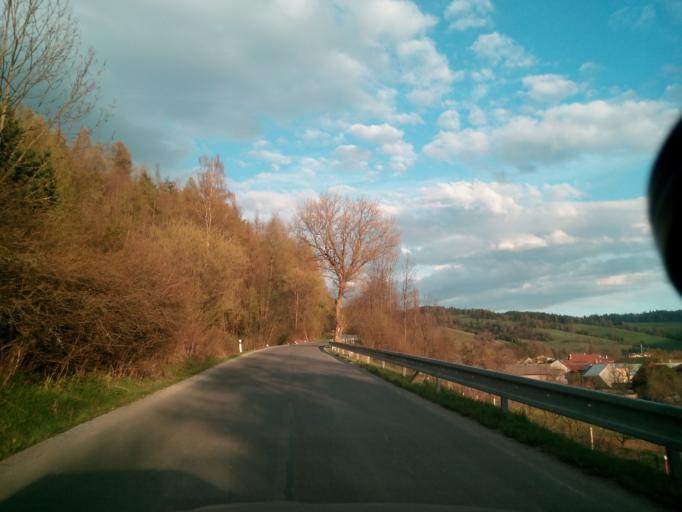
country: PL
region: Lesser Poland Voivodeship
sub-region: Powiat nowotarski
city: Niedzica
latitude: 49.3381
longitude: 20.2959
